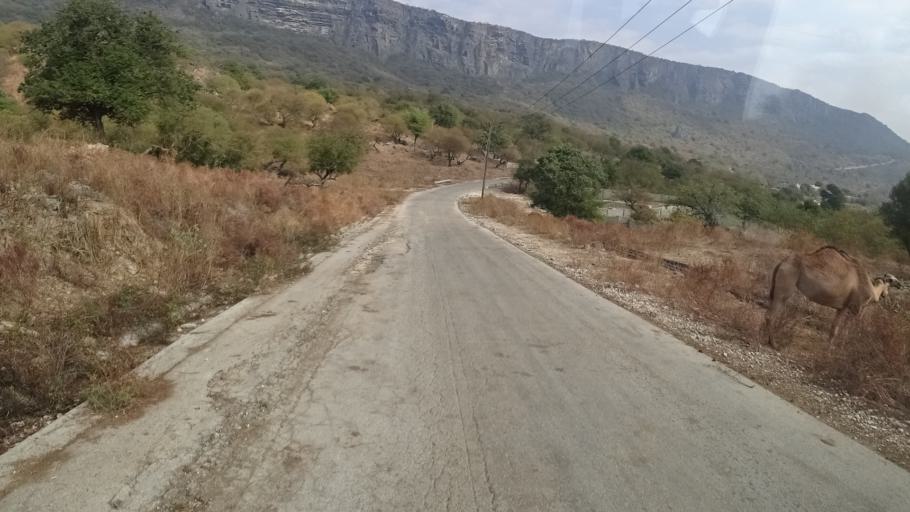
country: YE
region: Al Mahrah
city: Hawf
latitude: 16.7124
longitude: 53.2480
